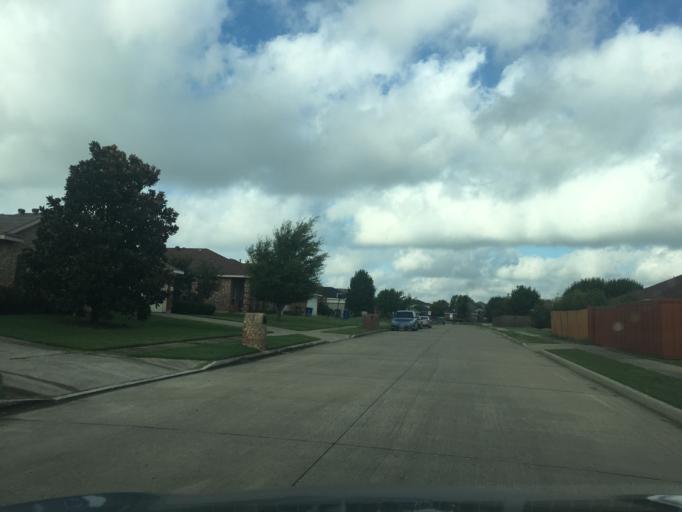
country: US
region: Texas
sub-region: Dallas County
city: Sachse
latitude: 32.9636
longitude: -96.5866
